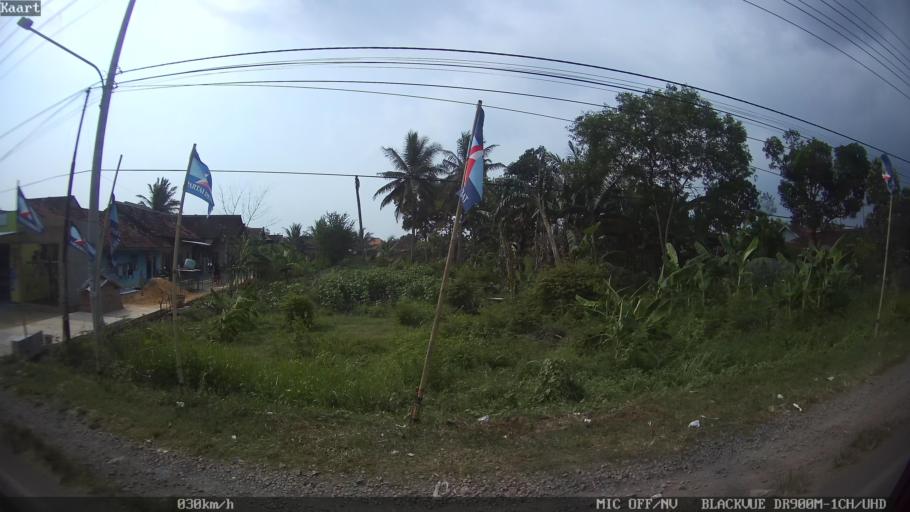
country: ID
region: Lampung
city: Gadingrejo
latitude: -5.3775
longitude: 105.0337
